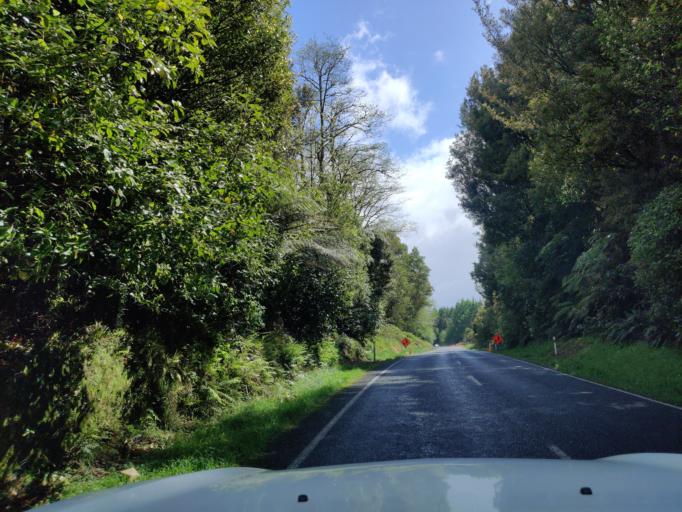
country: NZ
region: Bay of Plenty
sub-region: Rotorua District
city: Rotorua
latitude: -38.1788
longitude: 176.3259
